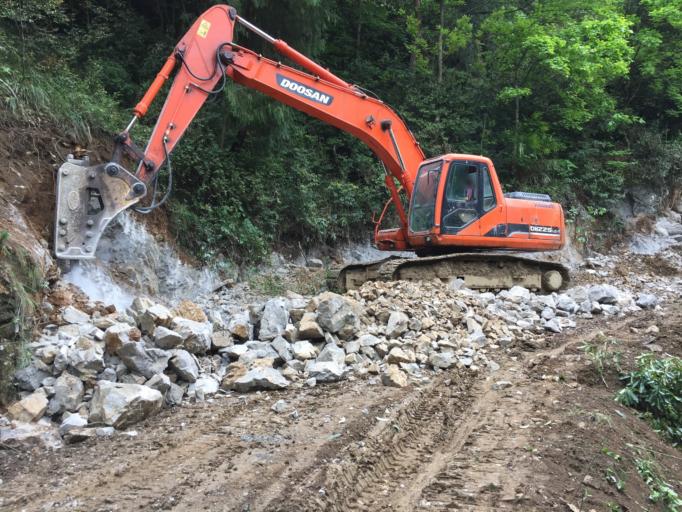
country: CN
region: Guizhou Sheng
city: Kuanping
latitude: 28.0114
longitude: 108.0700
